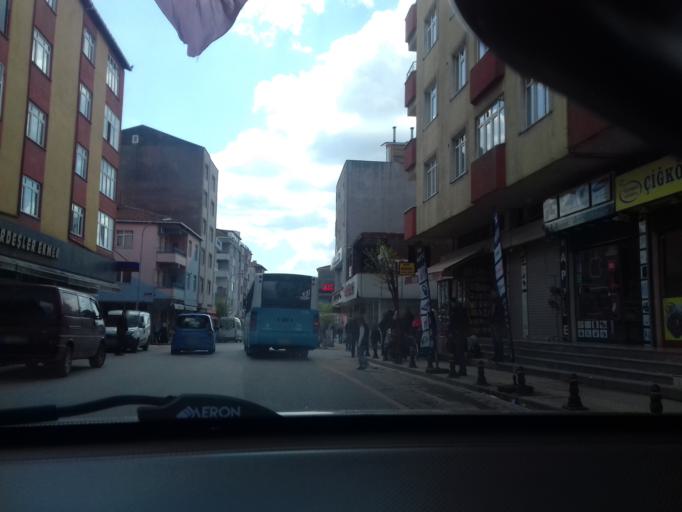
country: TR
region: Istanbul
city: Pendik
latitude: 40.8835
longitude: 29.2865
